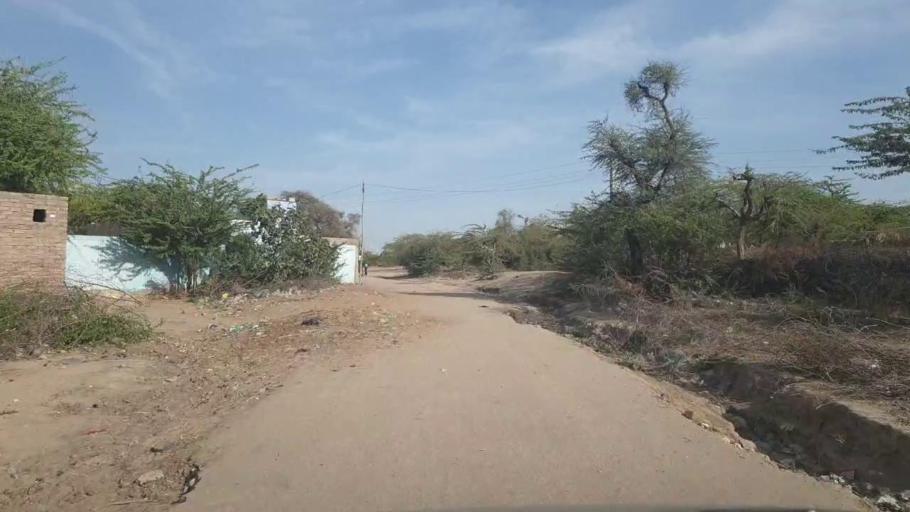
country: PK
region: Sindh
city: Nabisar
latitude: 25.0651
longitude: 69.6412
